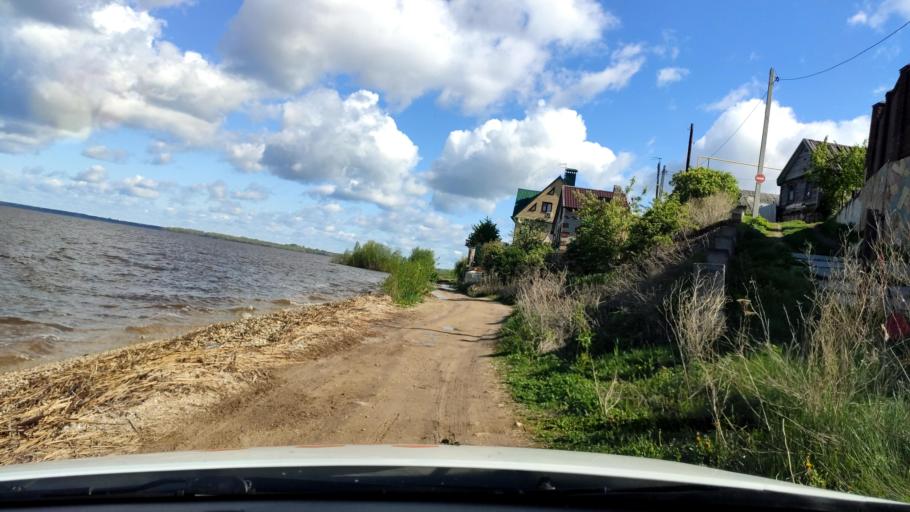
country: RU
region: Tatarstan
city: Sviyazhsk
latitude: 55.7686
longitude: 48.6859
